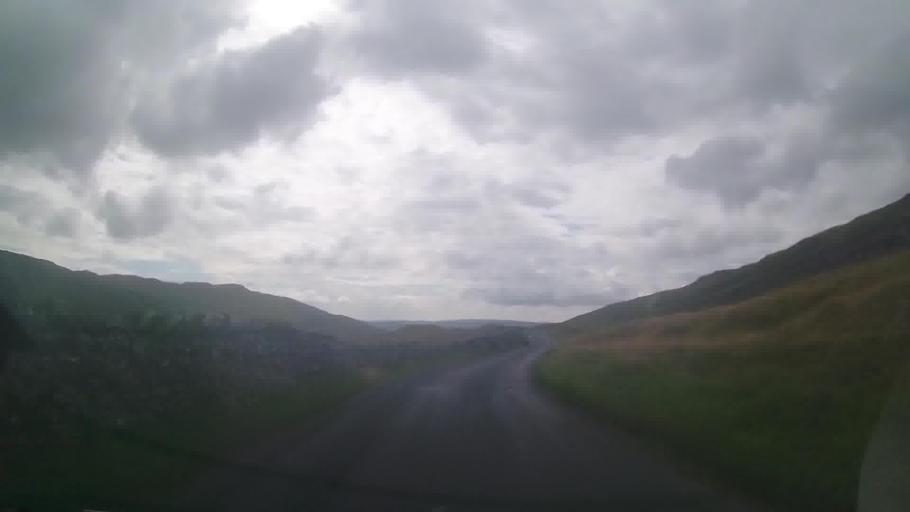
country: GB
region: England
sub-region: Cumbria
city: Ambleside
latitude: 54.4540
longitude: -2.9350
